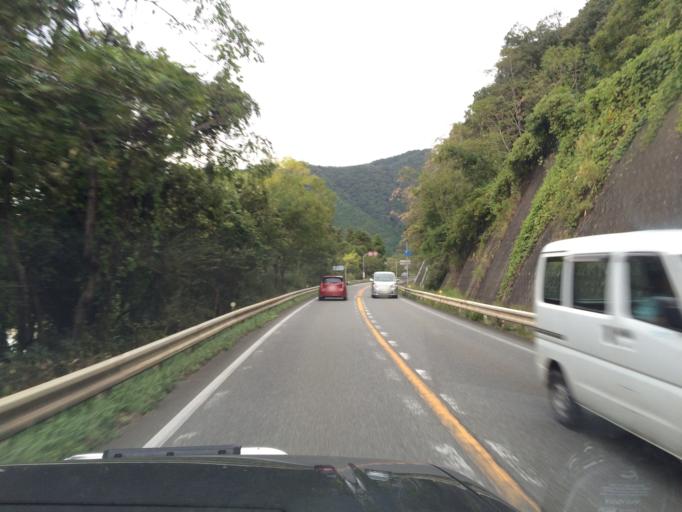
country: JP
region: Hyogo
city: Toyooka
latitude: 35.3693
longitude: 134.8198
